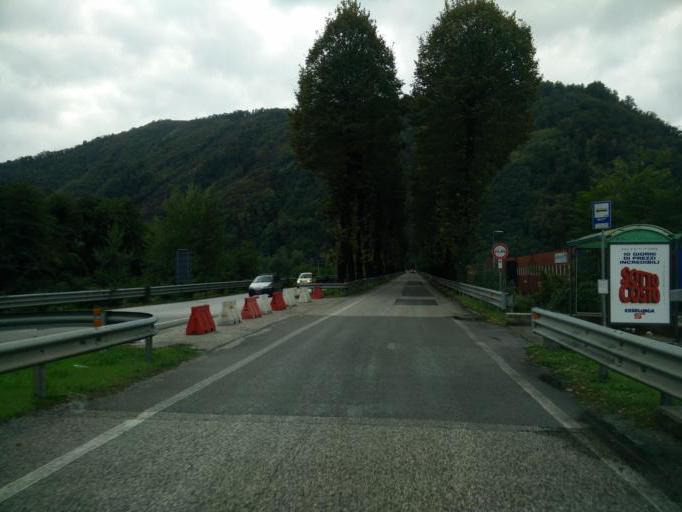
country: IT
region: Tuscany
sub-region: Provincia di Lucca
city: Valdottavo
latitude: 43.9426
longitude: 10.4961
